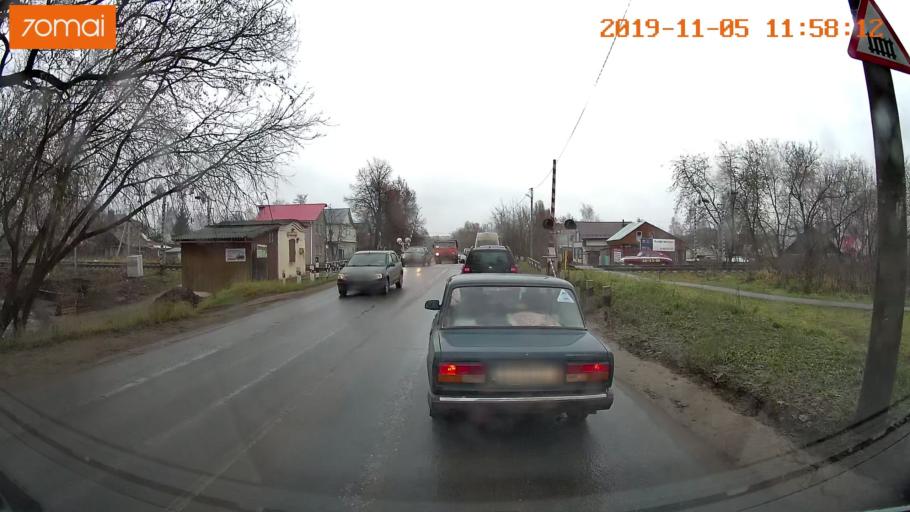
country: RU
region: Ivanovo
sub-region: Gorod Ivanovo
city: Ivanovo
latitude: 56.9813
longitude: 41.0392
